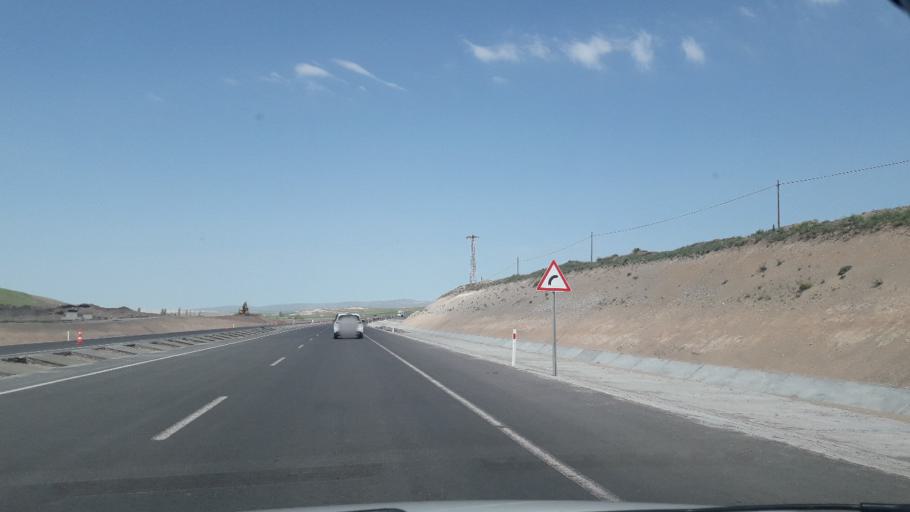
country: TR
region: Sivas
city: Deliktas
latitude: 39.2068
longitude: 37.2094
